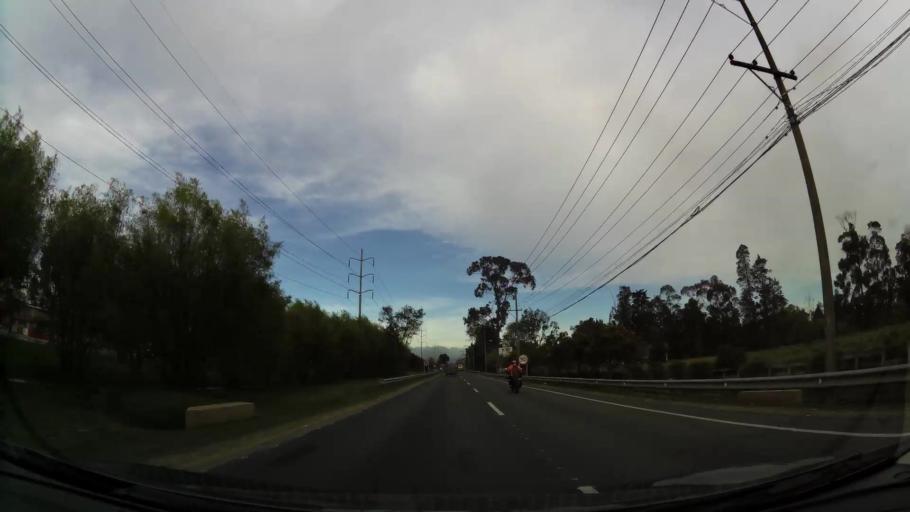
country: CO
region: Cundinamarca
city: Funza
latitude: 4.6969
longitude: -74.2128
